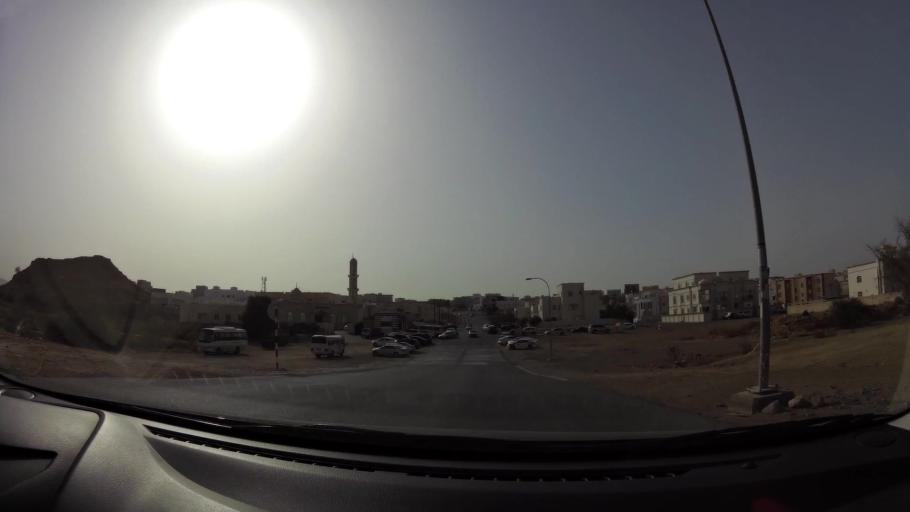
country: OM
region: Muhafazat Masqat
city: Bawshar
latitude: 23.5490
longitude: 58.3630
